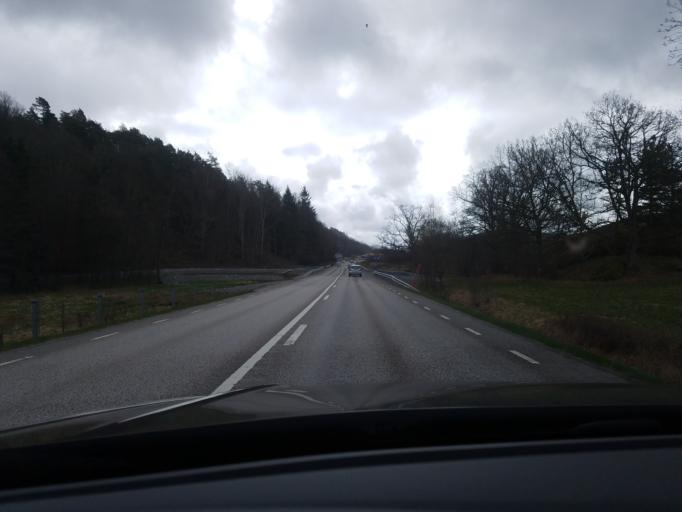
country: SE
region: Vaestra Goetaland
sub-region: Tjorns Kommun
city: Myggenas
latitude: 58.1354
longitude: 11.7156
